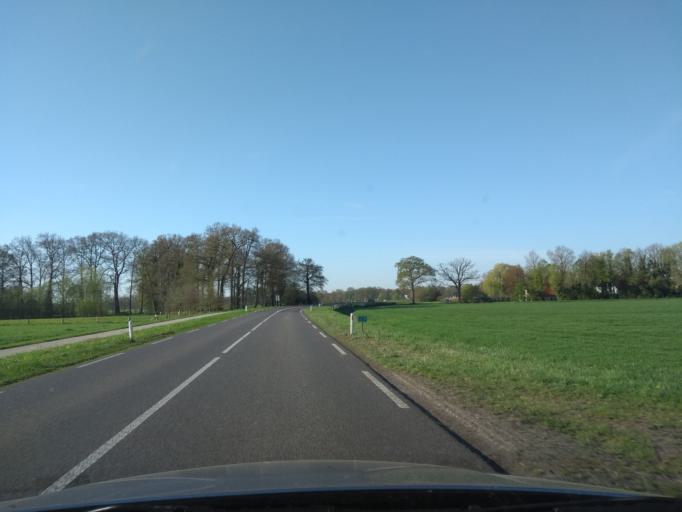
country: NL
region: Gelderland
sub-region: Berkelland
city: Neede
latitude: 52.1696
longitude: 6.6066
